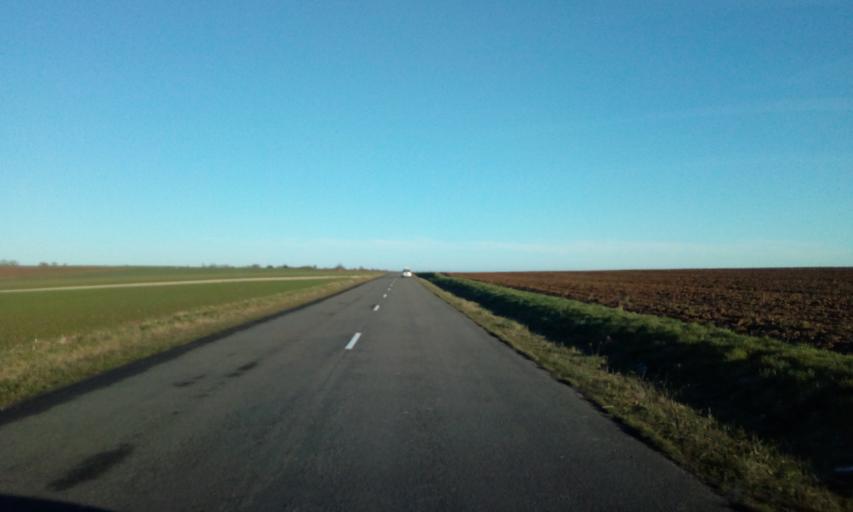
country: FR
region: Picardie
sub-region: Departement de l'Aisne
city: Rozoy-sur-Serre
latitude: 49.7004
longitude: 4.1929
